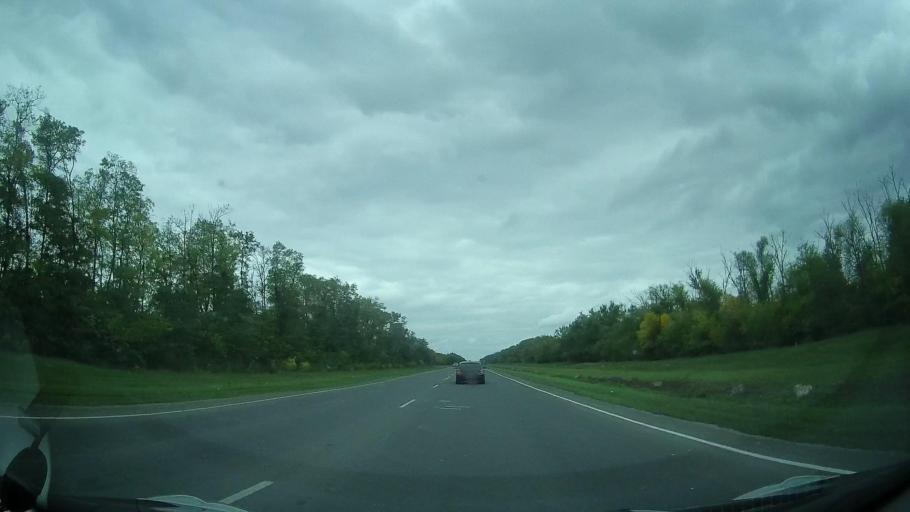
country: RU
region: Rostov
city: Yegorlykskaya
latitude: 46.5978
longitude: 40.6212
